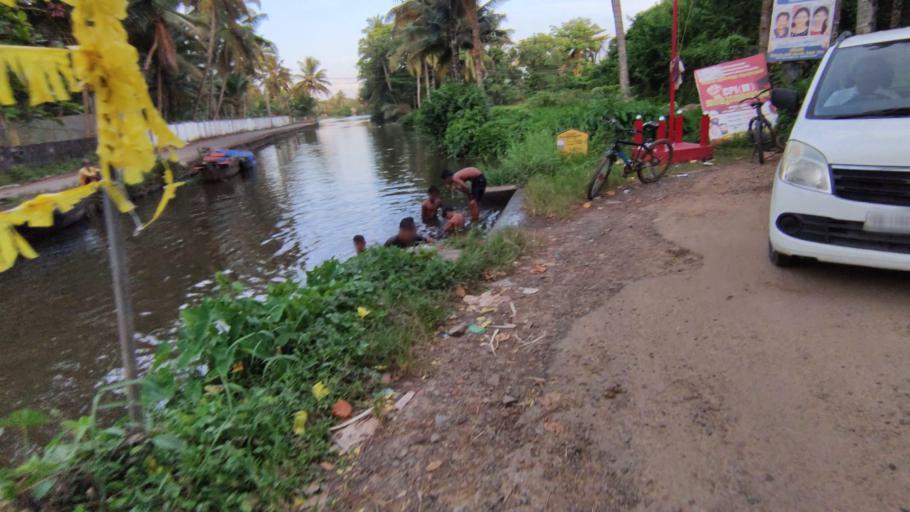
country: IN
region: Kerala
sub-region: Kottayam
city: Kottayam
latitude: 9.5797
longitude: 76.4391
